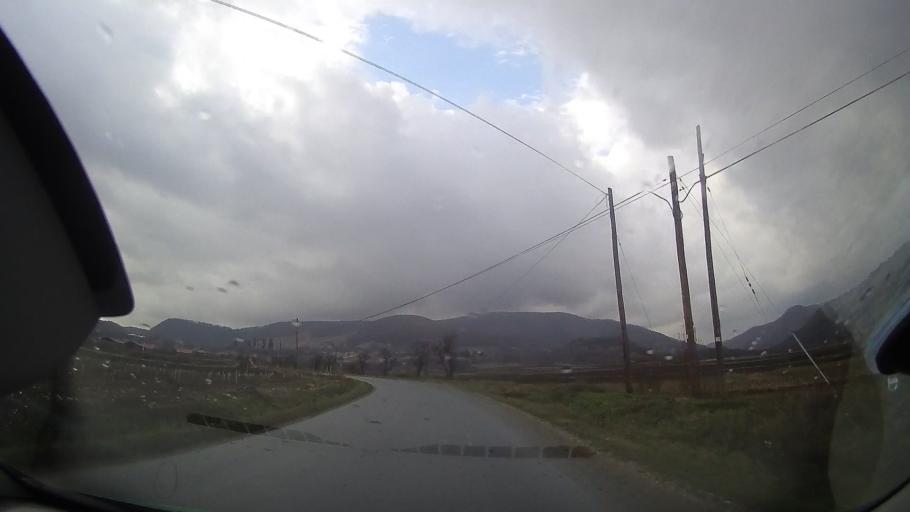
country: RO
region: Cluj
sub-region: Comuna Moldovenesti
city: Moldovenesti
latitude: 46.5065
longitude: 23.6688
